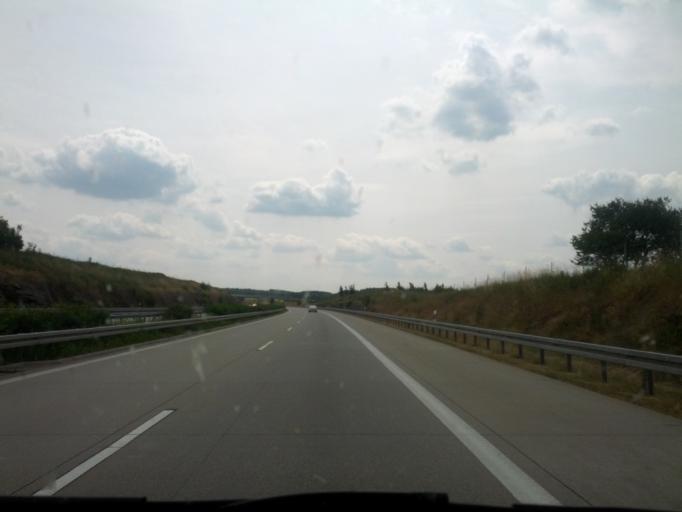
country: DE
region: Saxony
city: Liebstadt
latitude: 50.8135
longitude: 13.8835
